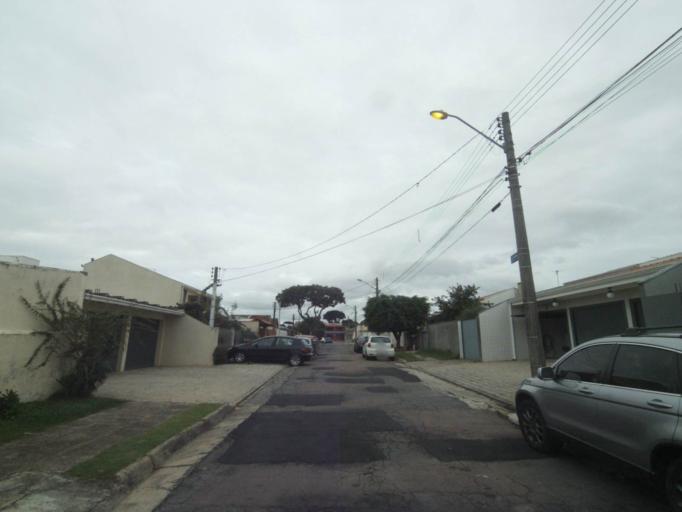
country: BR
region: Parana
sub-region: Curitiba
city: Curitiba
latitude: -25.4914
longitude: -49.2842
